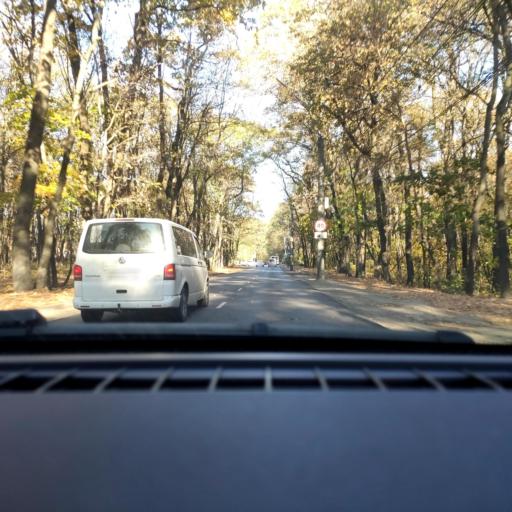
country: RU
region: Voronezj
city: Voronezh
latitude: 51.7192
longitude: 39.2244
